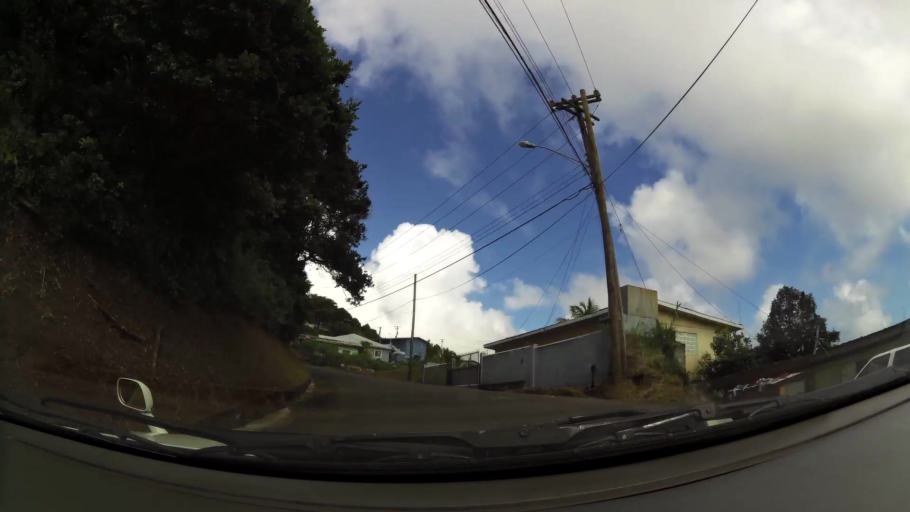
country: VC
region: Saint George
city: Kingstown
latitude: 13.1639
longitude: -61.1812
